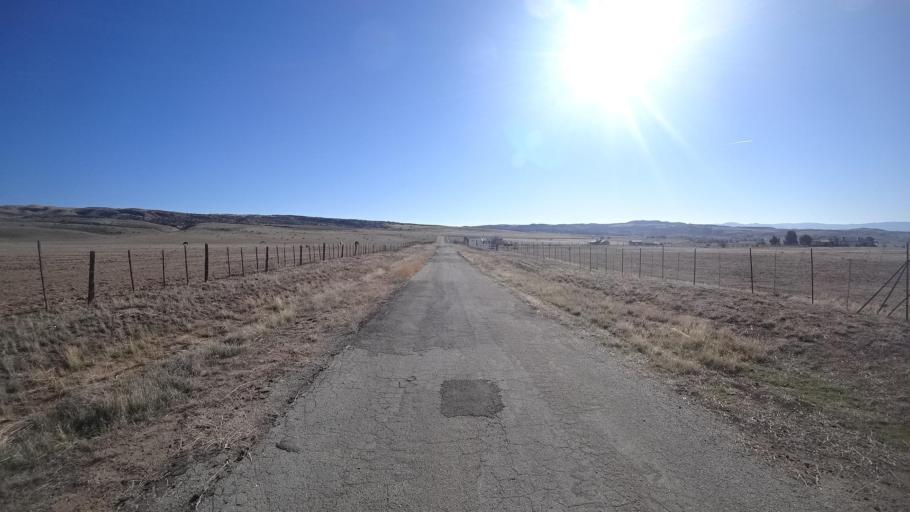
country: US
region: California
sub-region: Kern County
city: Maricopa
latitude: 34.9445
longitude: -119.4553
